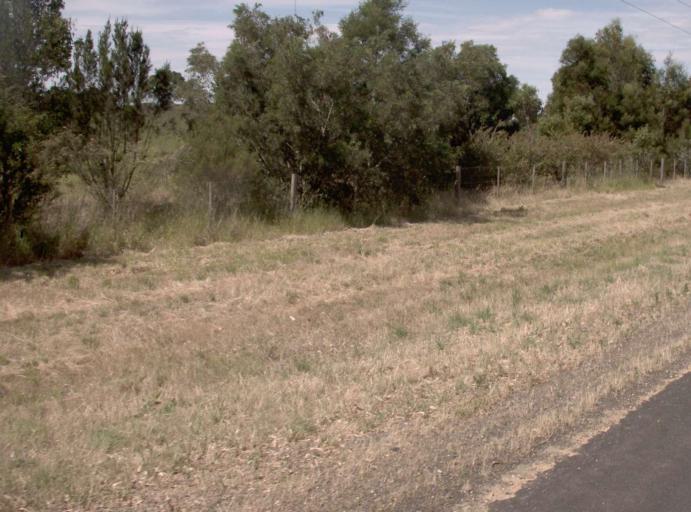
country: AU
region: Victoria
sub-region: Wellington
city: Sale
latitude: -37.9265
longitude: 147.2202
